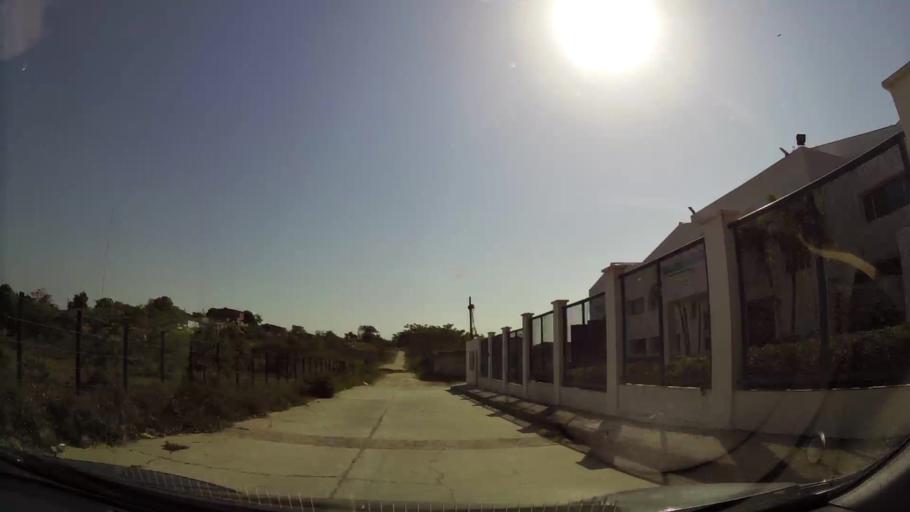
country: CO
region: Bolivar
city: Cartagena
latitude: 10.3693
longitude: -75.5035
